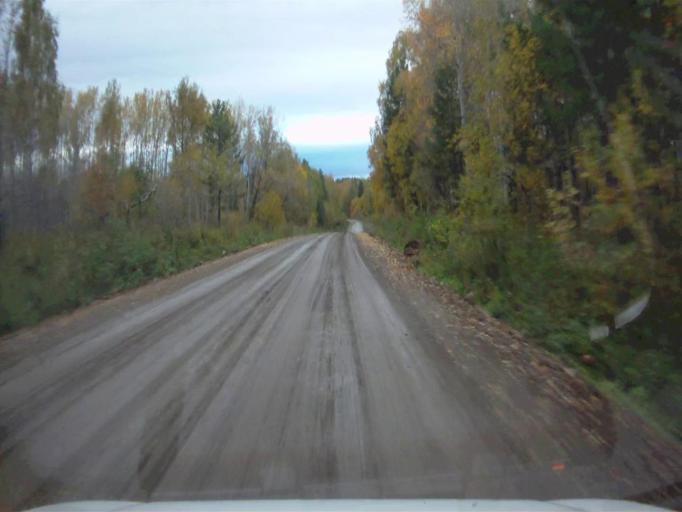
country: RU
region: Chelyabinsk
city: Nyazepetrovsk
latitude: 56.1164
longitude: 59.3680
